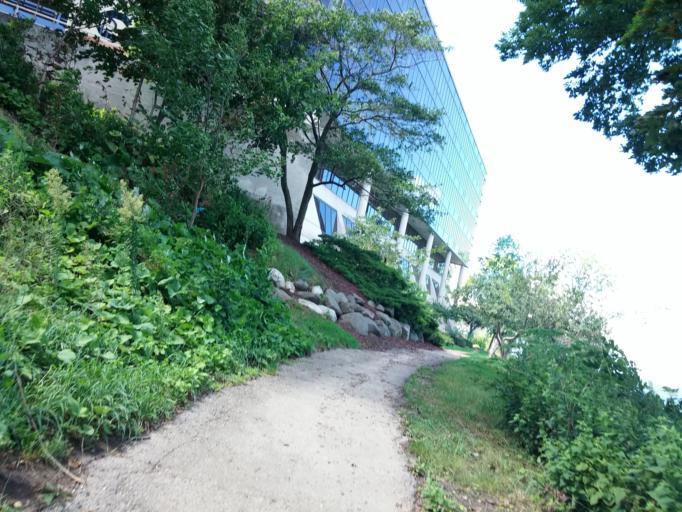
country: US
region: Wisconsin
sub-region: Dane County
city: Madison
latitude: 43.0806
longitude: -89.3859
